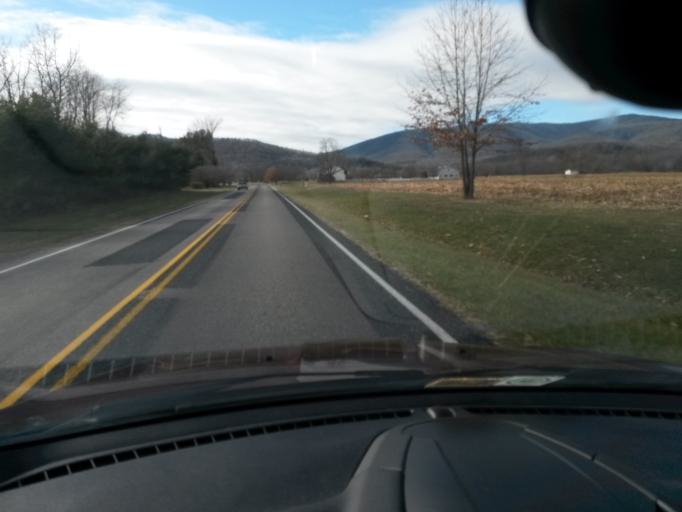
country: US
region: Virginia
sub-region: City of Staunton
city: Staunton
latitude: 38.2092
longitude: -79.2070
